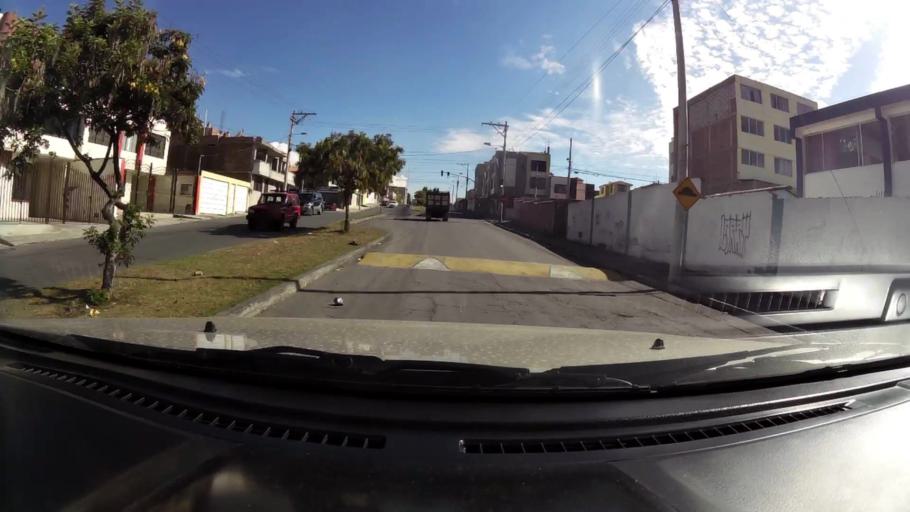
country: EC
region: Chimborazo
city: Riobamba
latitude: -1.6612
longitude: -78.6697
